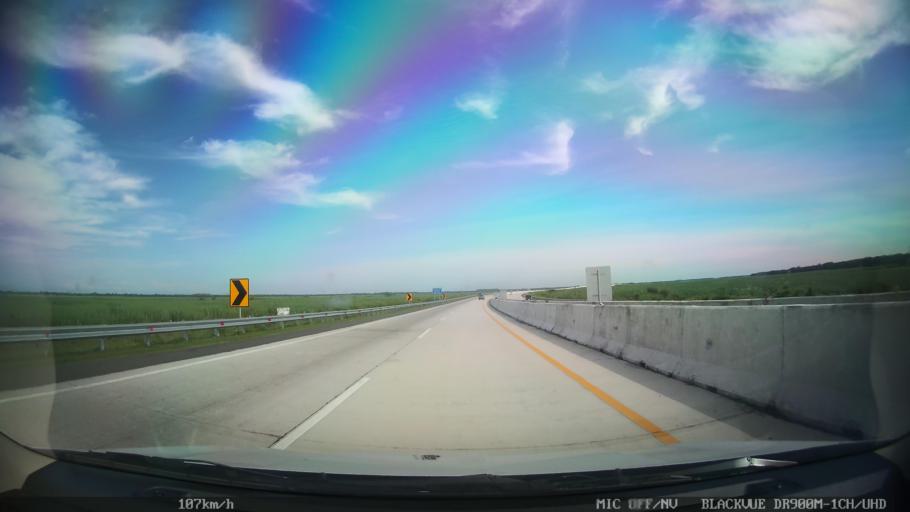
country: ID
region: North Sumatra
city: Binjai
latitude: 3.6552
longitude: 98.5347
